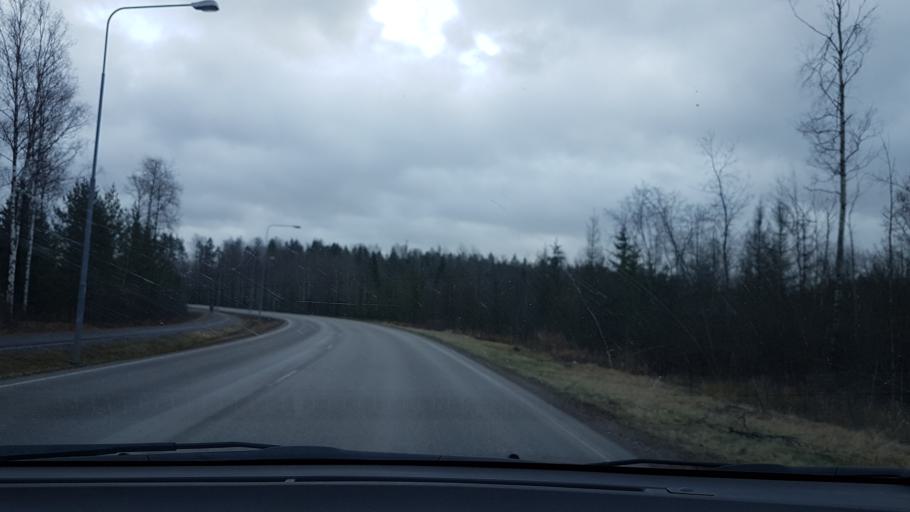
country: FI
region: Uusimaa
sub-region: Helsinki
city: Tuusula
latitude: 60.3725
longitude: 25.0630
